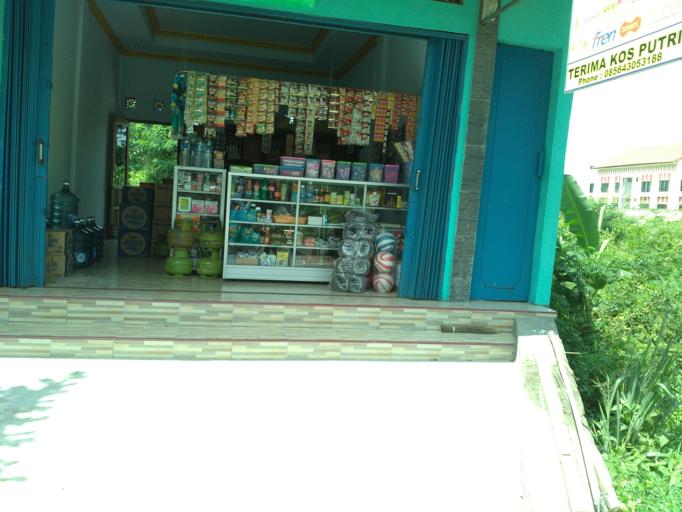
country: ID
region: Central Java
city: Klaten
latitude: -7.7162
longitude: 110.5841
